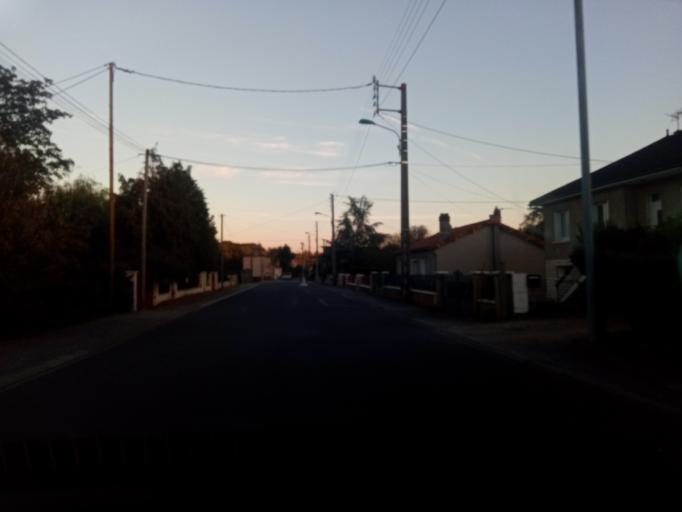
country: FR
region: Poitou-Charentes
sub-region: Departement de la Vienne
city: Montmorillon
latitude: 46.4146
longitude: 0.8784
